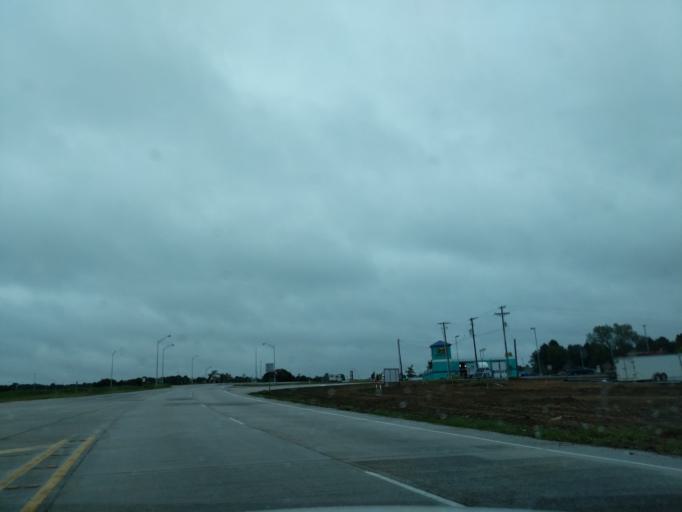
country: US
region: Louisiana
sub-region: Caddo Parish
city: Greenwood
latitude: 32.4447
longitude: -93.8999
